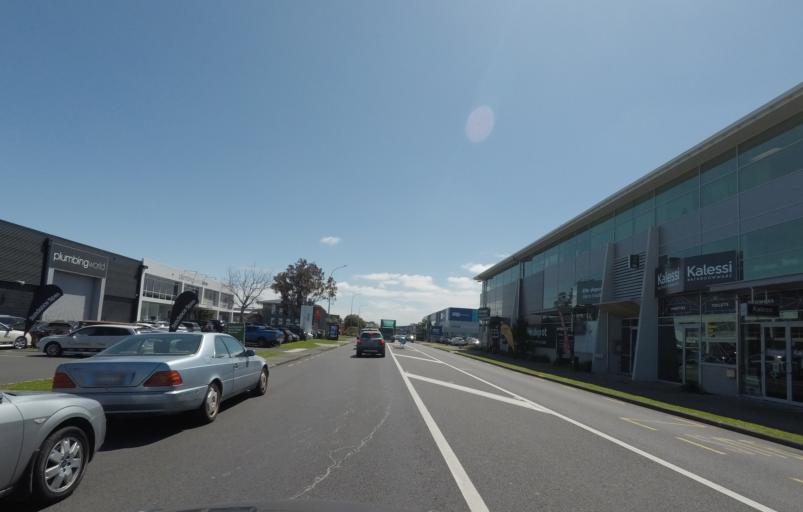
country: NZ
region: Auckland
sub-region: Auckland
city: Tamaki
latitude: -36.8927
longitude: 174.8374
